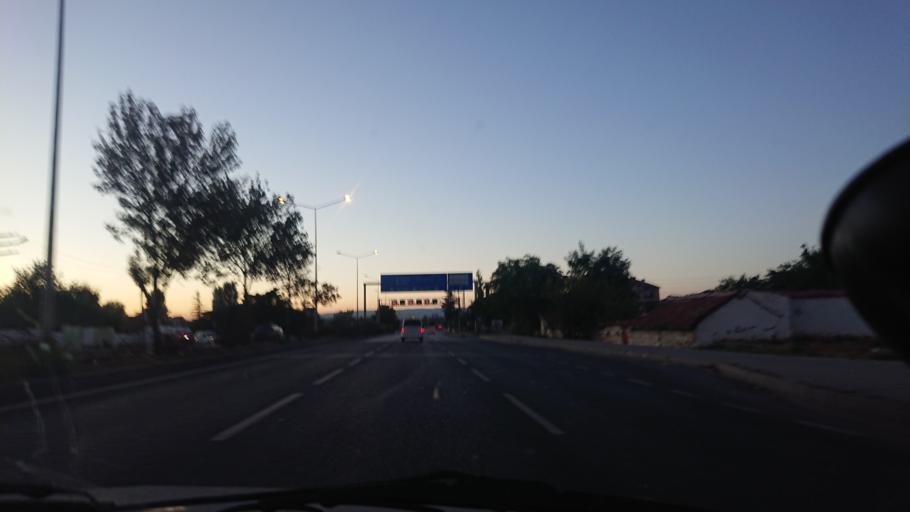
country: TR
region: Eskisehir
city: Eskisehir
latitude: 39.7702
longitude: 30.5610
